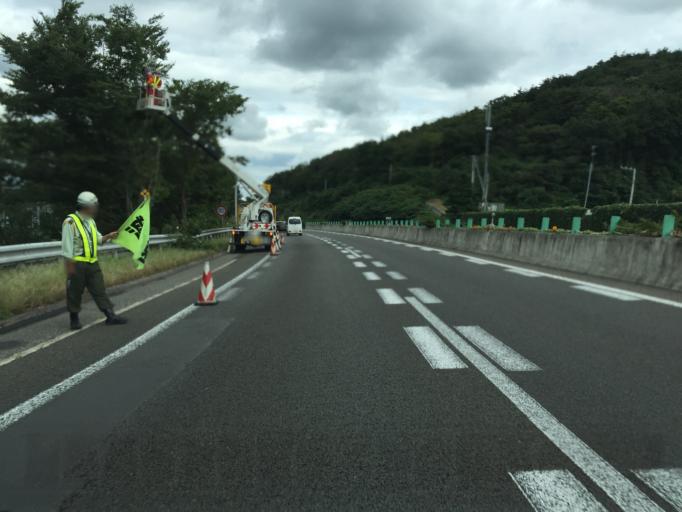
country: JP
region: Miyagi
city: Shiroishi
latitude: 37.9399
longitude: 140.6118
